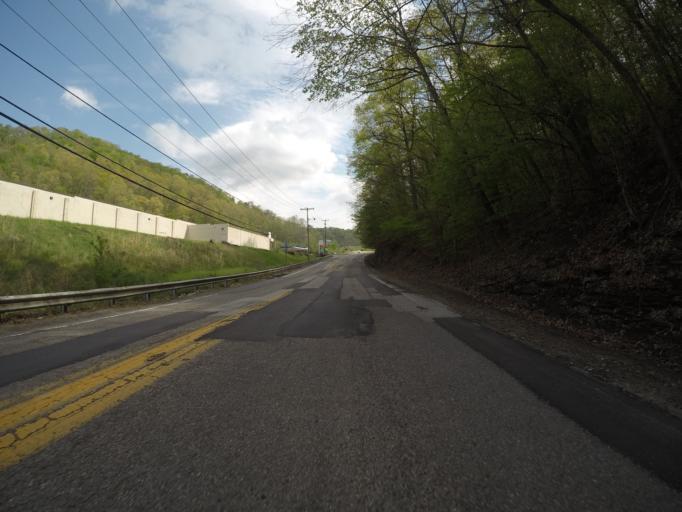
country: US
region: West Virginia
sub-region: Boone County
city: Madison
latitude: 38.0872
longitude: -81.8388
